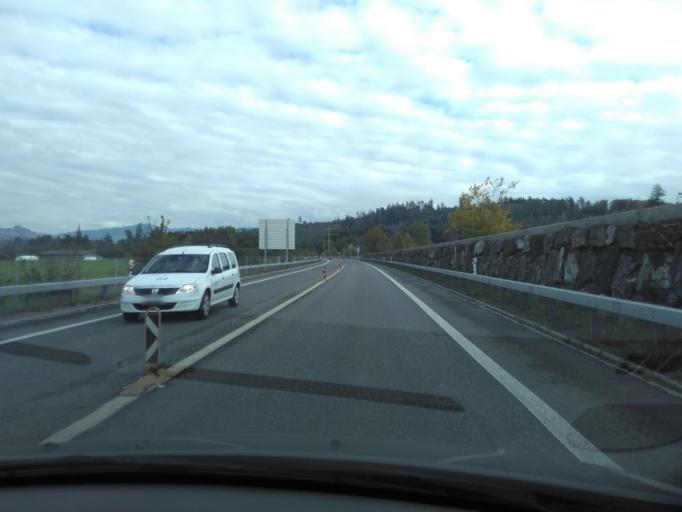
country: CH
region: Zurich
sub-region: Bezirk Hinwil
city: Rueti / Dorfzentrum, Suedl. Teil
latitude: 47.2274
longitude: 8.8749
